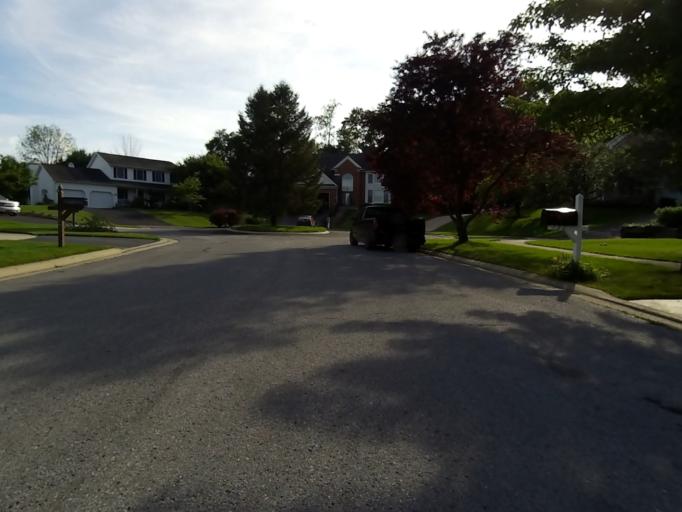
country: US
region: Pennsylvania
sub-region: Centre County
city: Park Forest Village
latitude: 40.8132
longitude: -77.9445
